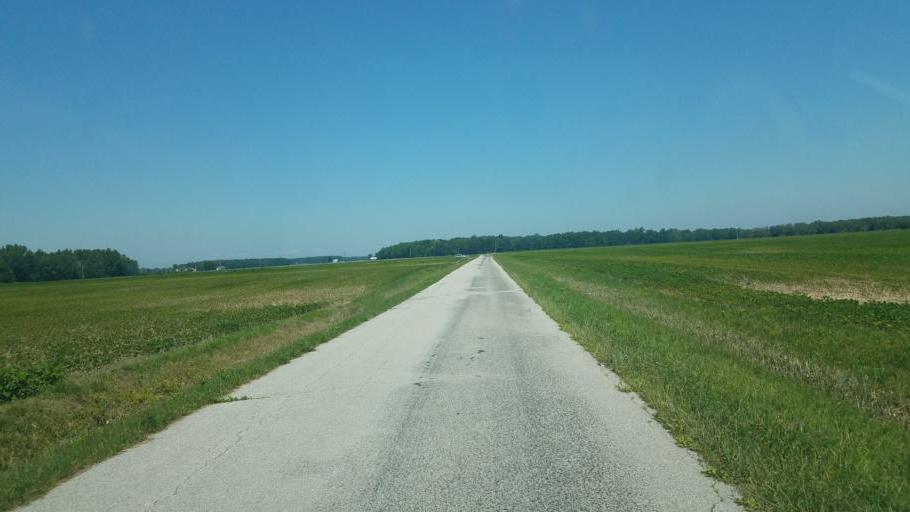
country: US
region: Ohio
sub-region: Sandusky County
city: Clyde
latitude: 41.3806
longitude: -82.9926
